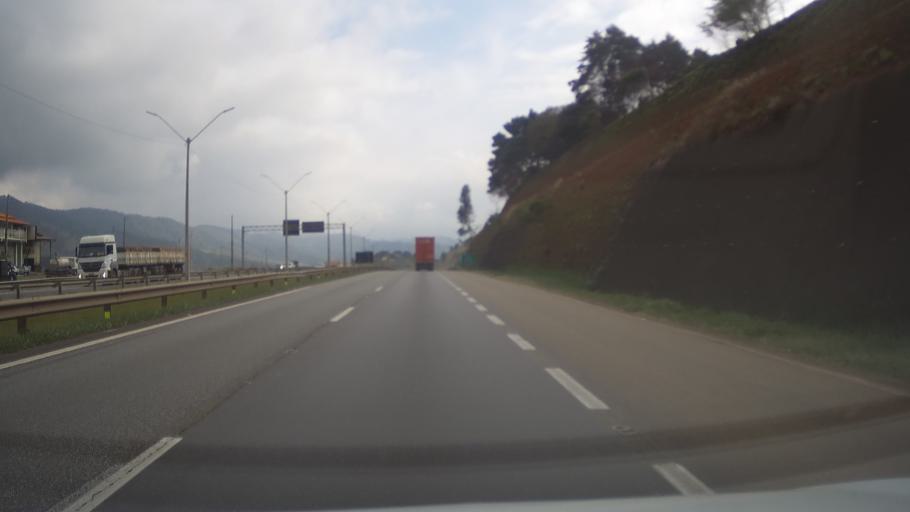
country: BR
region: Minas Gerais
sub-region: Extrema
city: Extrema
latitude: -22.9023
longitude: -46.4209
